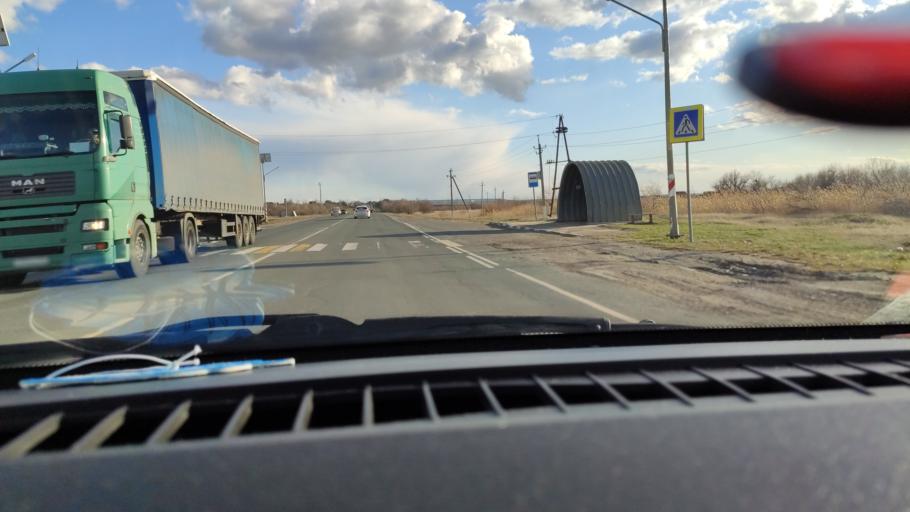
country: RU
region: Saratov
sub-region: Saratovskiy Rayon
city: Saratov
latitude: 51.6884
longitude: 46.0046
